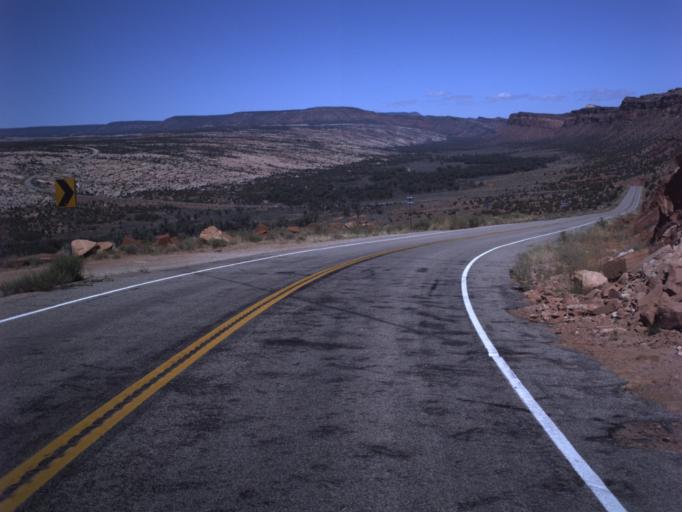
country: US
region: Utah
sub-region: San Juan County
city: Blanding
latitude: 37.4975
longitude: -109.6477
